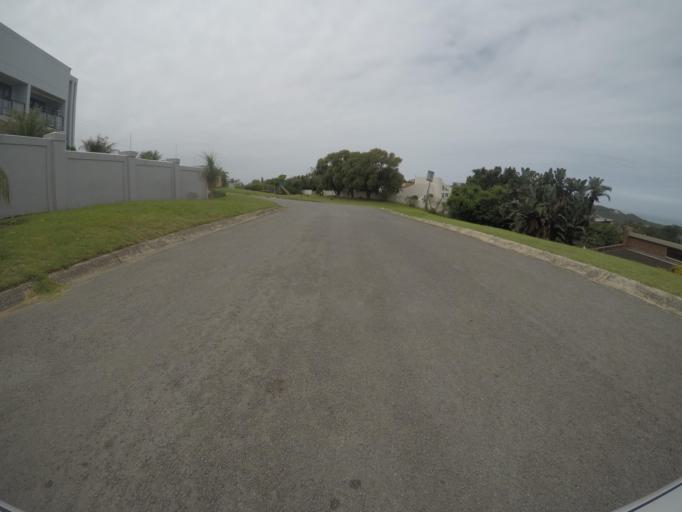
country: ZA
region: Eastern Cape
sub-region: Buffalo City Metropolitan Municipality
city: East London
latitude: -32.9787
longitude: 27.9441
